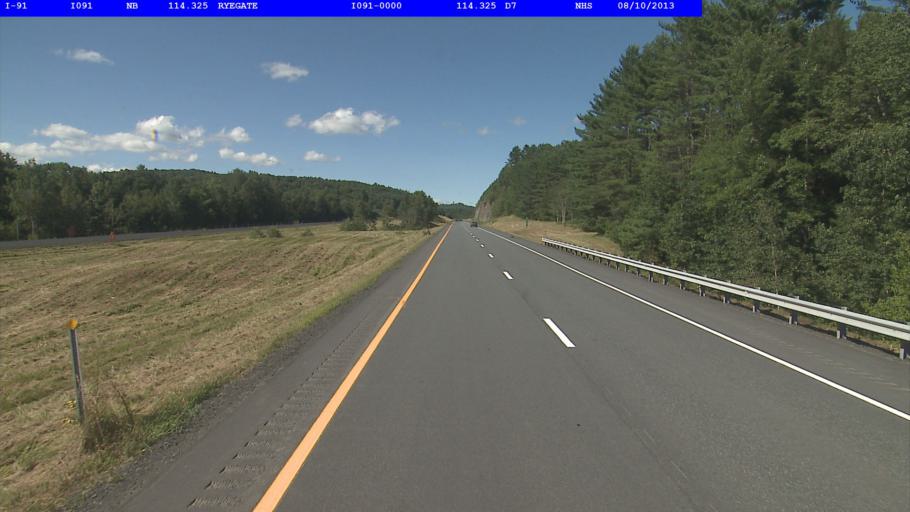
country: US
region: New Hampshire
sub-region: Grafton County
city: Woodsville
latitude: 44.2151
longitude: -72.0670
